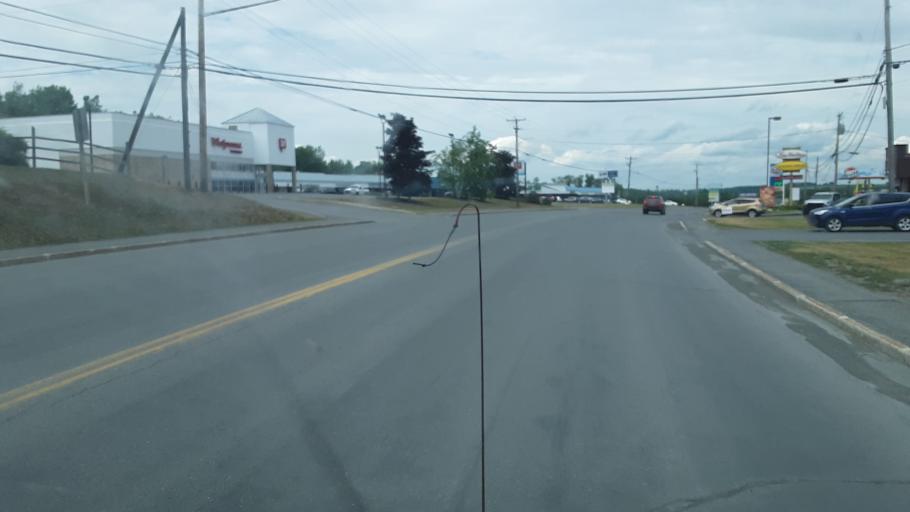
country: US
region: Maine
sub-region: Aroostook County
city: Caribou
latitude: 46.8677
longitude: -68.0048
